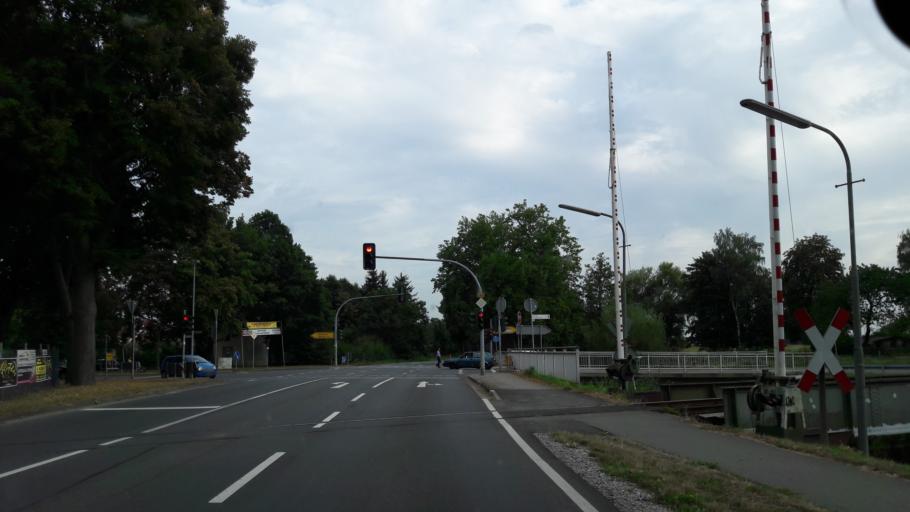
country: DE
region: Lower Saxony
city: Bockenem
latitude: 52.0094
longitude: 10.1237
